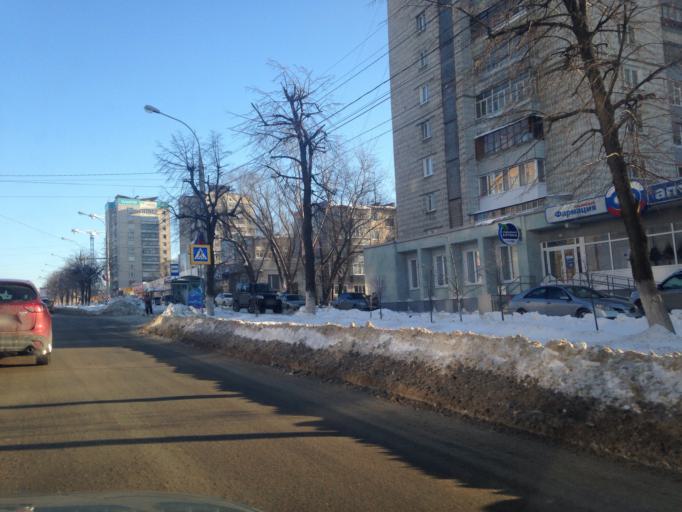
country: RU
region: Ulyanovsk
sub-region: Ulyanovskiy Rayon
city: Ulyanovsk
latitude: 54.3070
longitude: 48.3822
